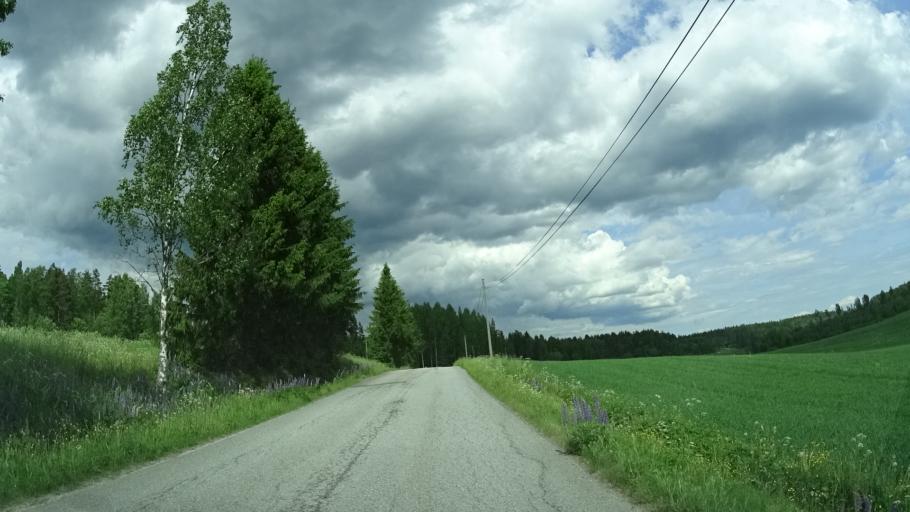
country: FI
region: Uusimaa
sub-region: Helsinki
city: Siuntio
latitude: 60.1945
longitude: 24.2177
